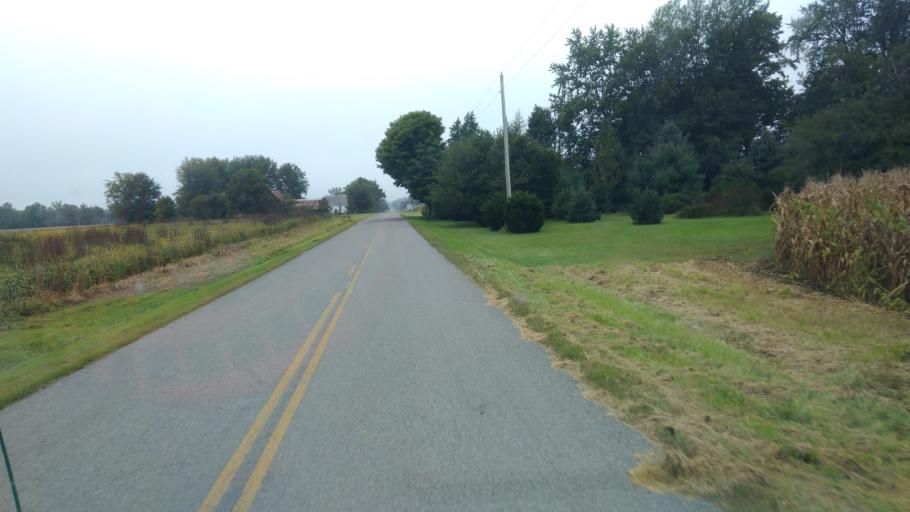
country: US
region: Ohio
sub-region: Logan County
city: Northwood
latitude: 40.4768
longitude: -83.5941
